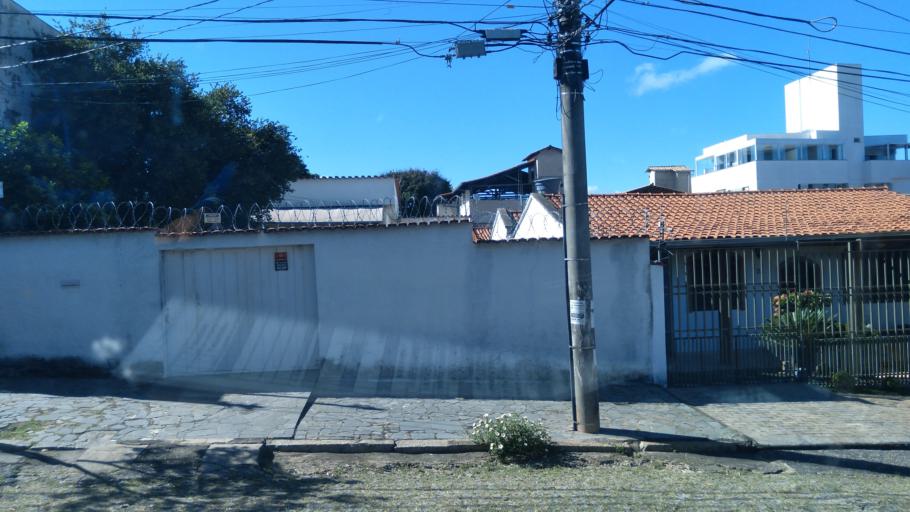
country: BR
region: Minas Gerais
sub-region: Belo Horizonte
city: Belo Horizonte
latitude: -19.8832
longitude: -43.9118
